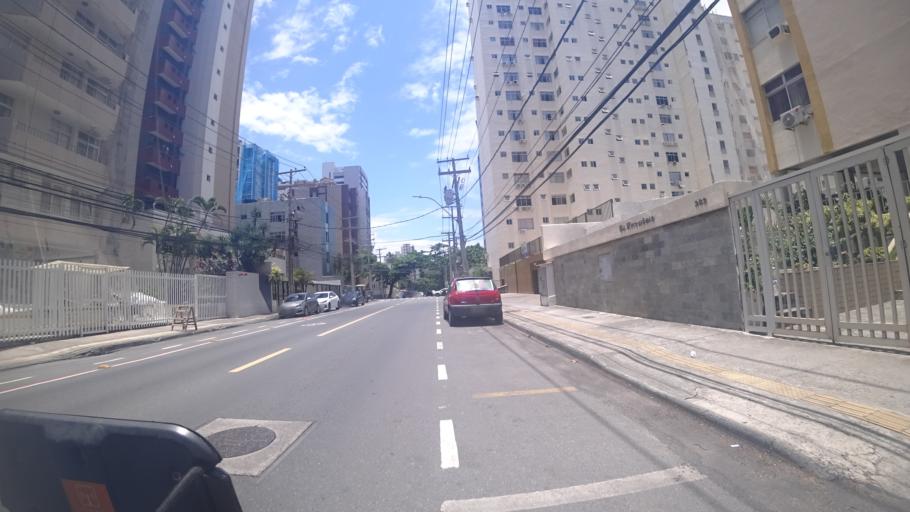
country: BR
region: Bahia
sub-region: Salvador
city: Salvador
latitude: -13.0074
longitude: -38.4643
